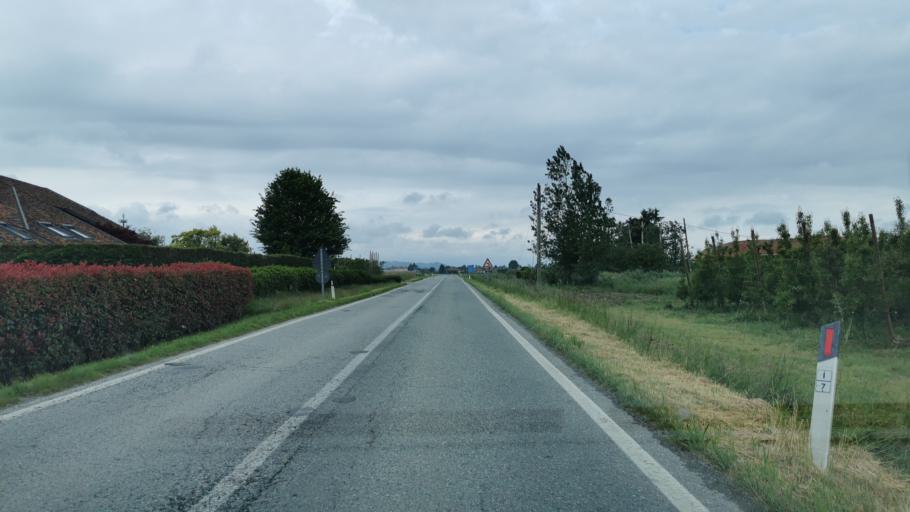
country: IT
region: Piedmont
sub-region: Provincia di Cuneo
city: Lagnasco
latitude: 44.6052
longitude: 7.5917
